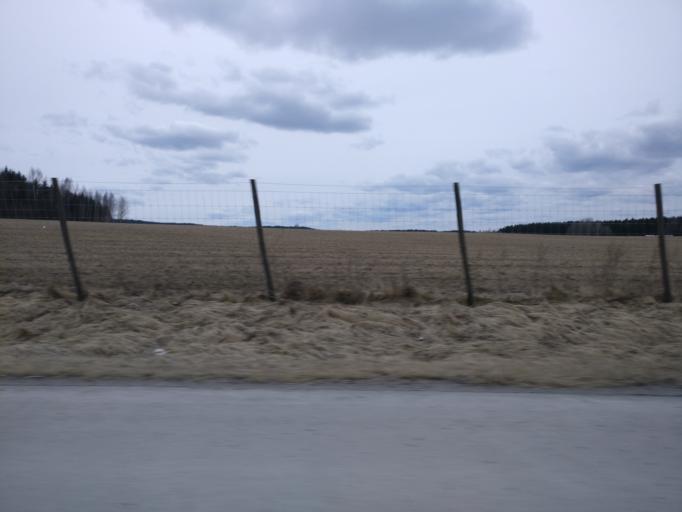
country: FI
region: Haeme
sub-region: Haemeenlinna
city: Janakkala
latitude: 60.8754
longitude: 24.5754
